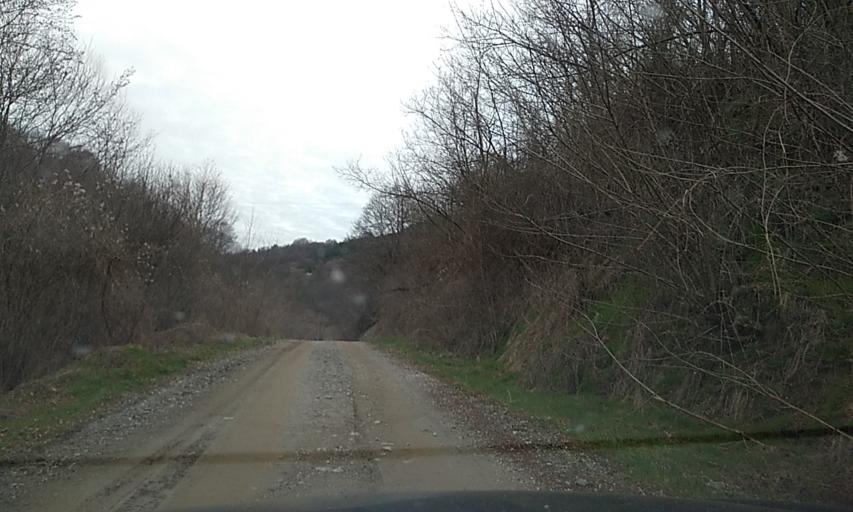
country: MK
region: Kriva Palanka
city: Kriva Palanka
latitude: 42.3408
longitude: 22.3689
